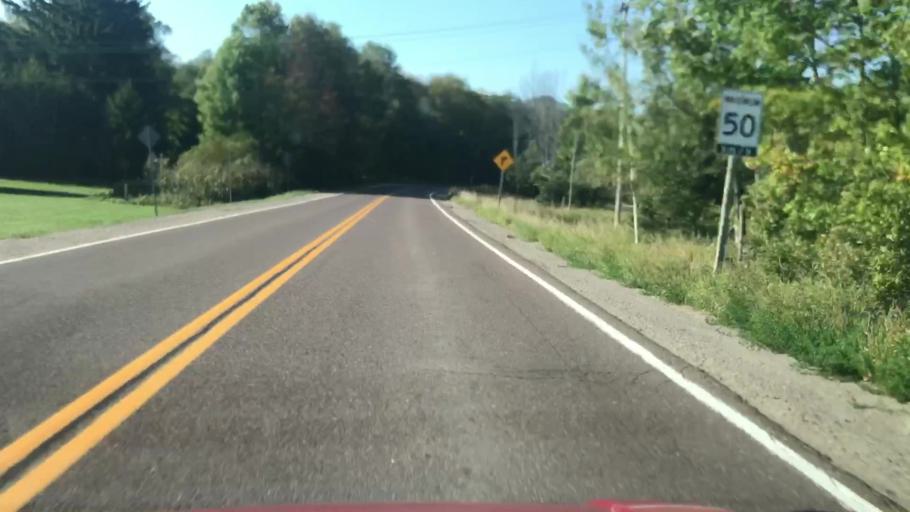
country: US
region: Michigan
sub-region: Chippewa County
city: Sault Ste. Marie
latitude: 46.2798
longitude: -84.0313
